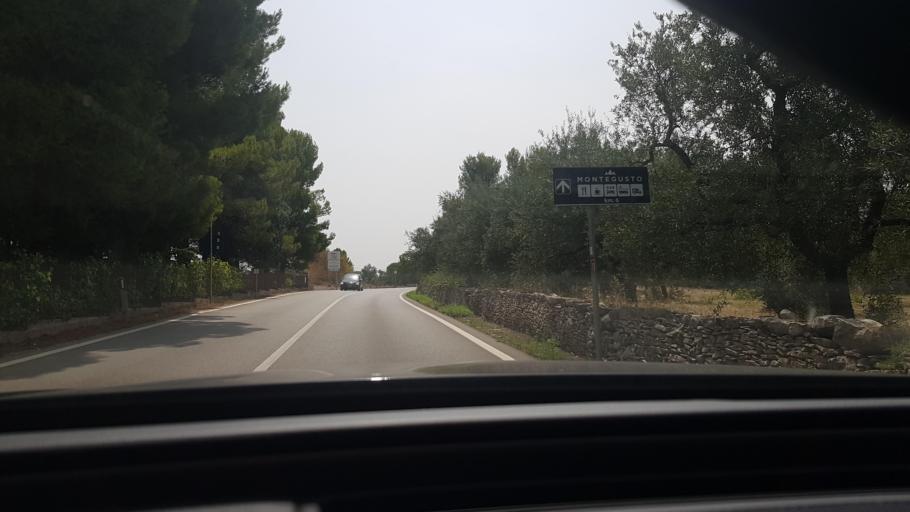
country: IT
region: Apulia
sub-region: Provincia di Barletta - Andria - Trani
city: Andria
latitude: 41.1351
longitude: 16.2907
